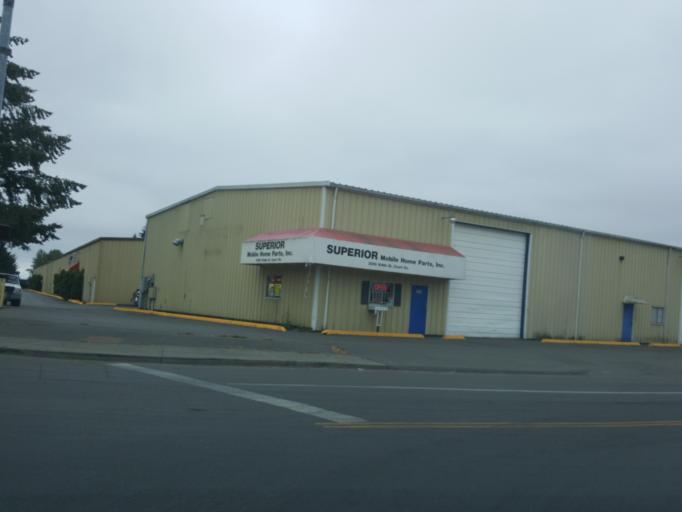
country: US
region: Washington
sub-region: Pierce County
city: Parkland
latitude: 47.1628
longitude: -122.4673
